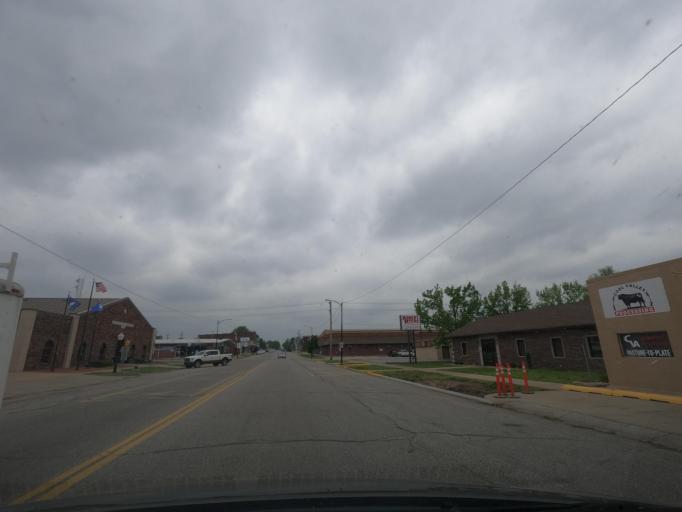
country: US
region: Kansas
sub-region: Cherokee County
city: Columbus
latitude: 37.1709
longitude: -94.8393
